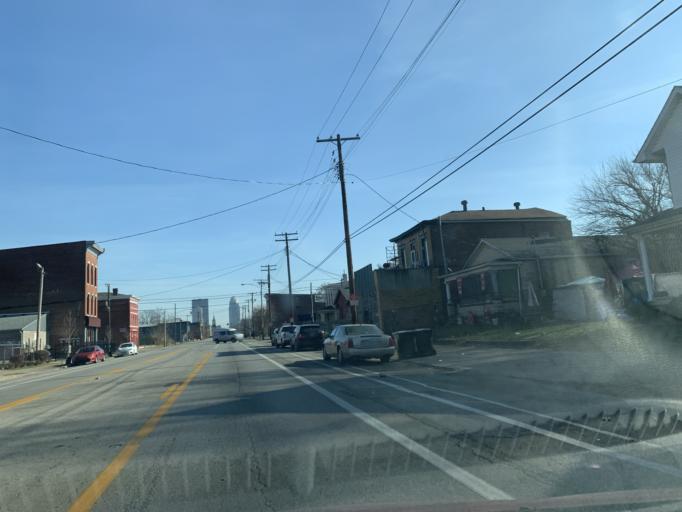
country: US
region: Kentucky
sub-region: Jefferson County
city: Louisville
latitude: 38.2581
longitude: -85.7827
